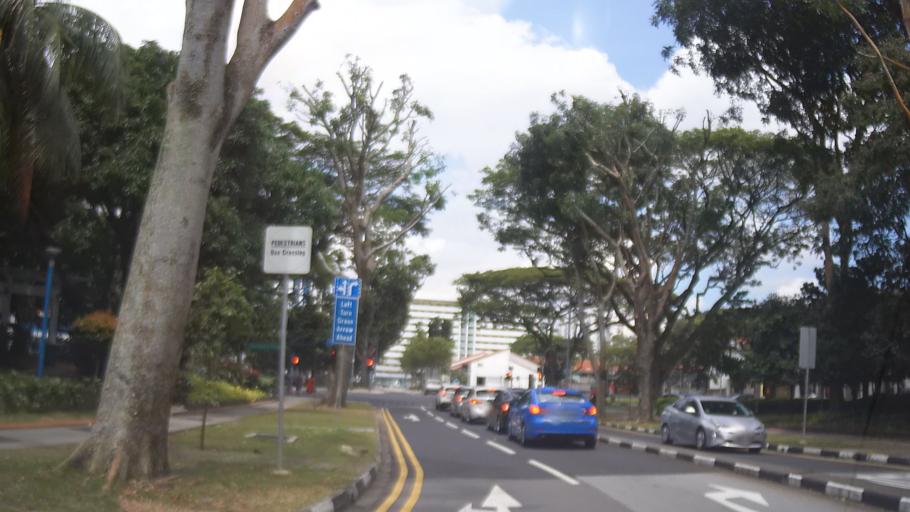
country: SG
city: Singapore
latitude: 1.3180
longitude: 103.8857
